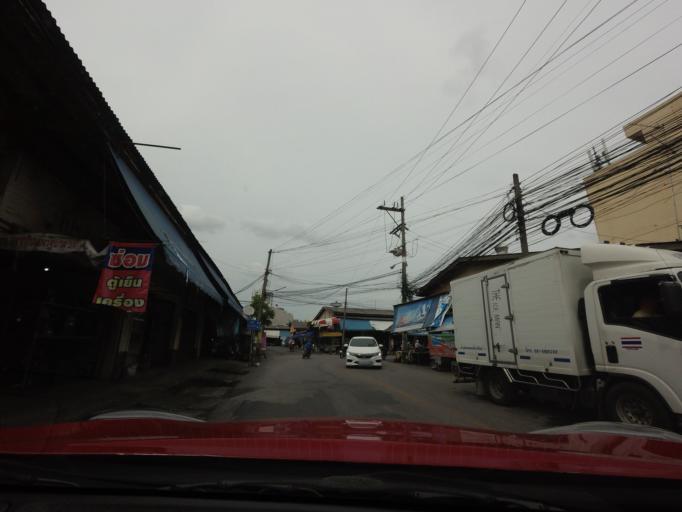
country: TH
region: Songkhla
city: Hat Yai
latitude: 6.9957
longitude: 100.4745
